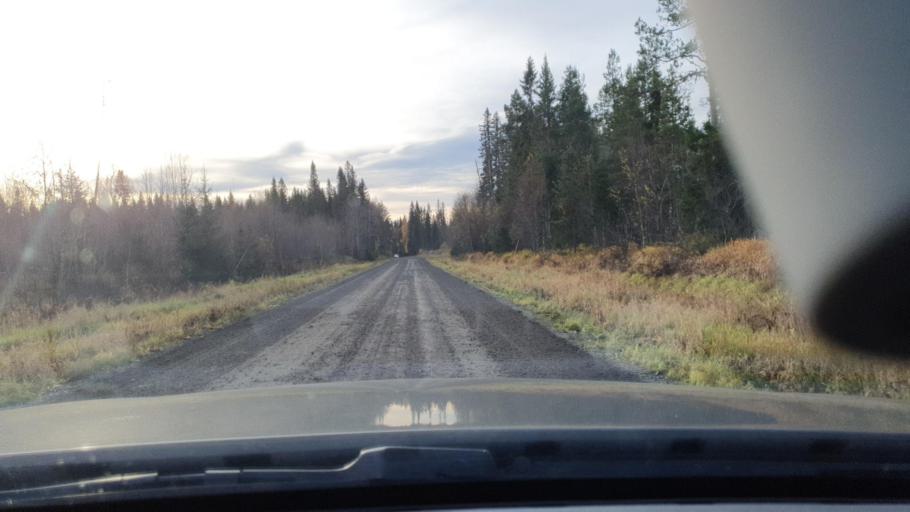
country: SE
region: Jaemtland
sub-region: Stroemsunds Kommun
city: Stroemsund
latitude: 63.5203
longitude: 15.6372
